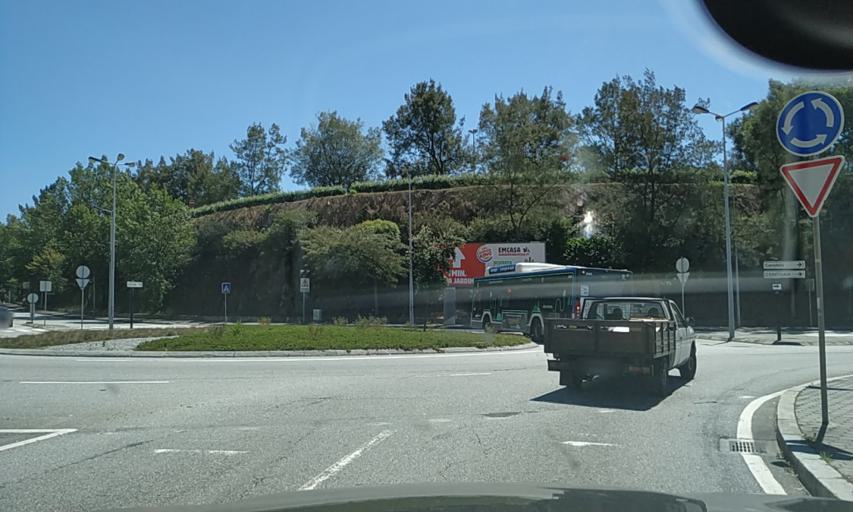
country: PT
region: Porto
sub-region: Vila Nova de Gaia
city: Canidelo
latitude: 41.1395
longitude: -8.6413
